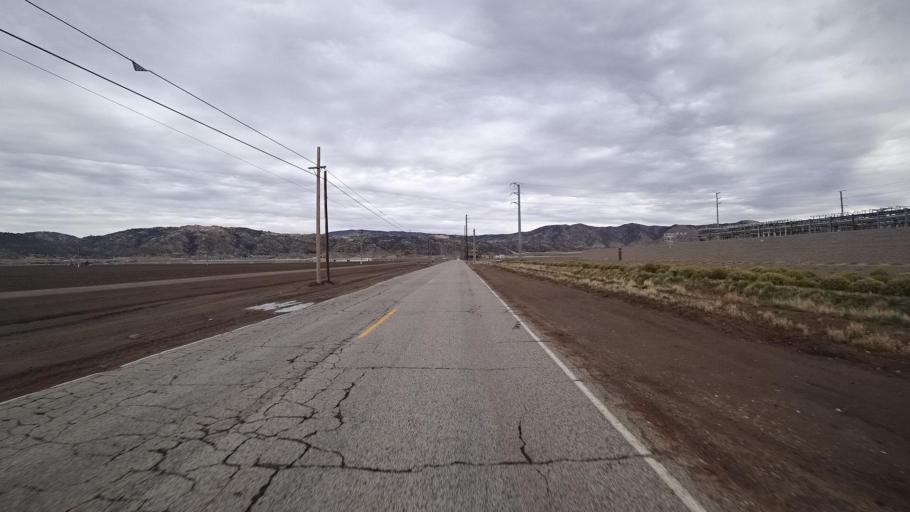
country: US
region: California
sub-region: Kern County
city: Stallion Springs
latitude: 35.1006
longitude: -118.6021
